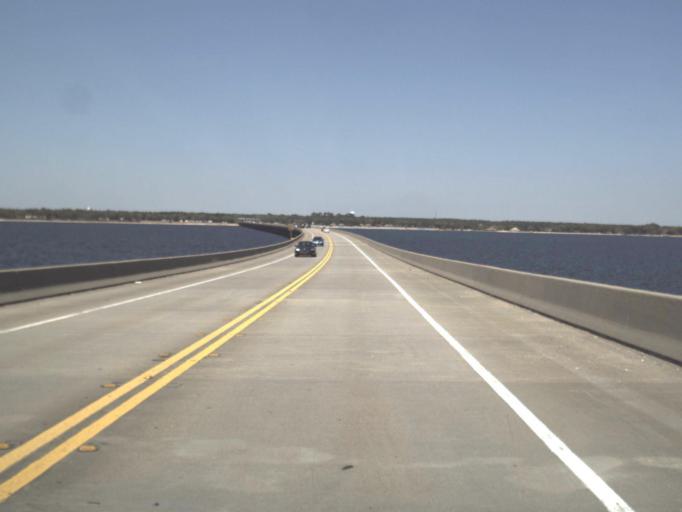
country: US
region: Florida
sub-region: Walton County
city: Miramar Beach
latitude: 30.4388
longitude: -86.4167
